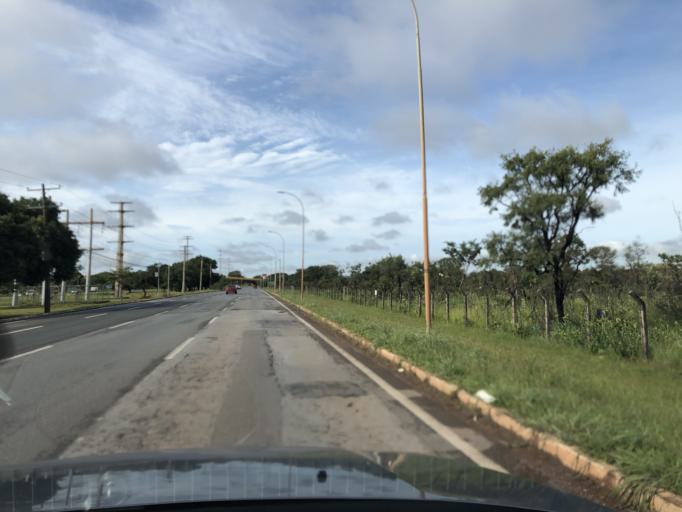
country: BR
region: Federal District
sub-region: Brasilia
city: Brasilia
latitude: -15.7804
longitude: -47.9404
